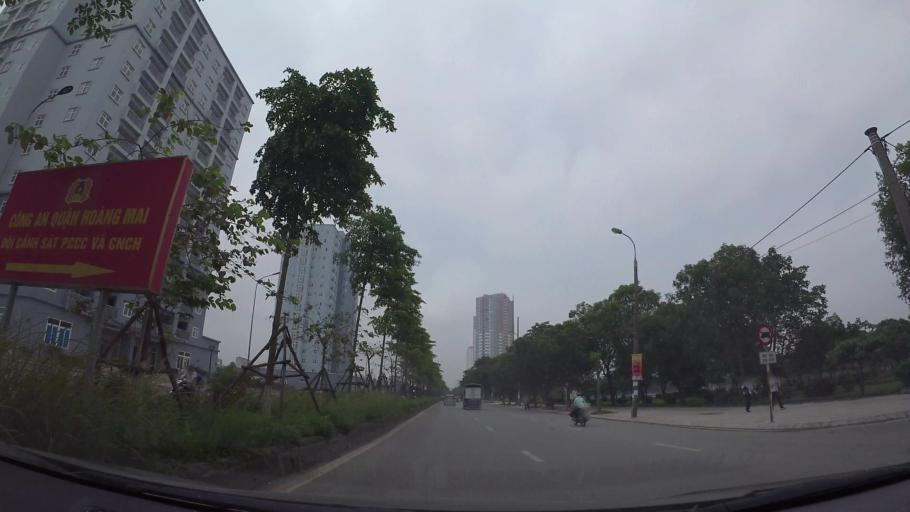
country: VN
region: Ha Noi
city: Hai BaTrung
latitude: 20.9835
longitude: 105.8572
